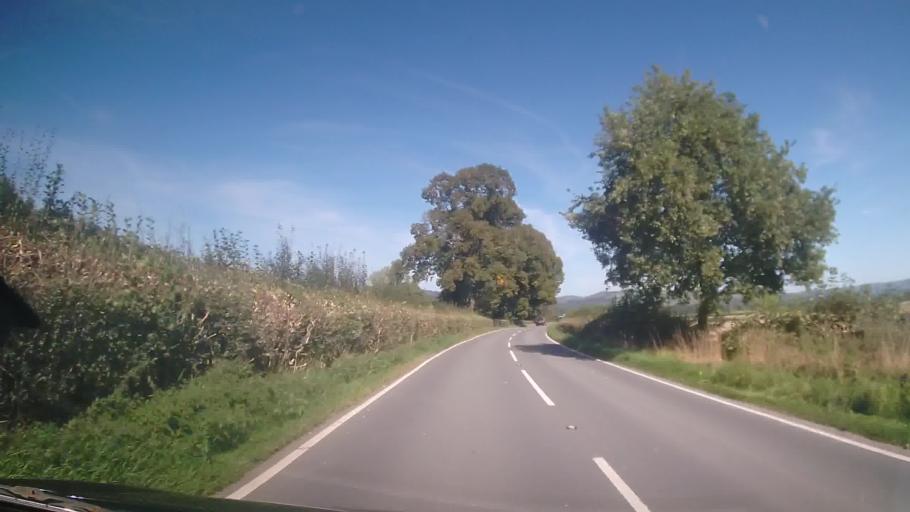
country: GB
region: England
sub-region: Shropshire
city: Lydham
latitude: 52.5029
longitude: -2.9846
